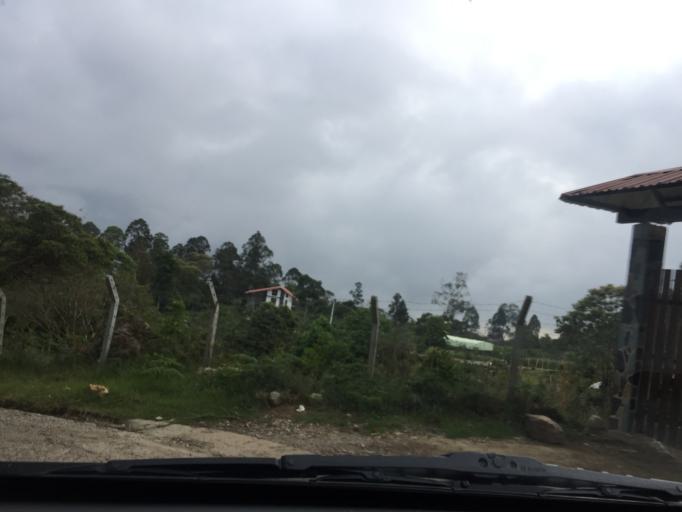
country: CO
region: Cundinamarca
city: Bojaca
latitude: 4.6813
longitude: -74.3767
